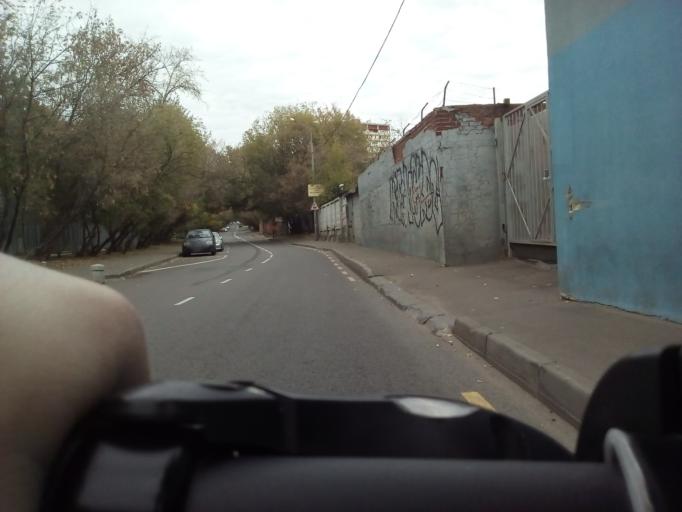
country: RU
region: Moscow
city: Lefortovo
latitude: 55.7855
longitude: 37.7107
